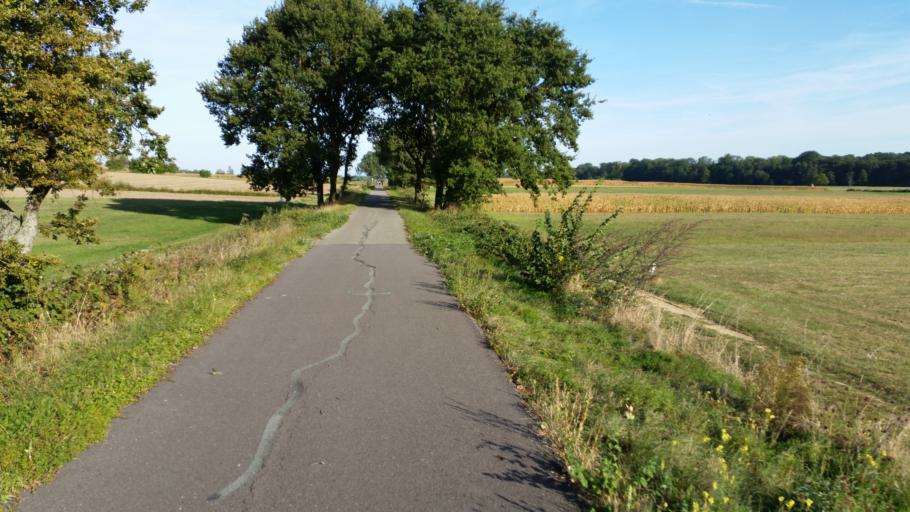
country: FR
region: Alsace
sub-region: Departement du Bas-Rhin
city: Betschdorf
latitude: 48.8971
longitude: 7.8762
